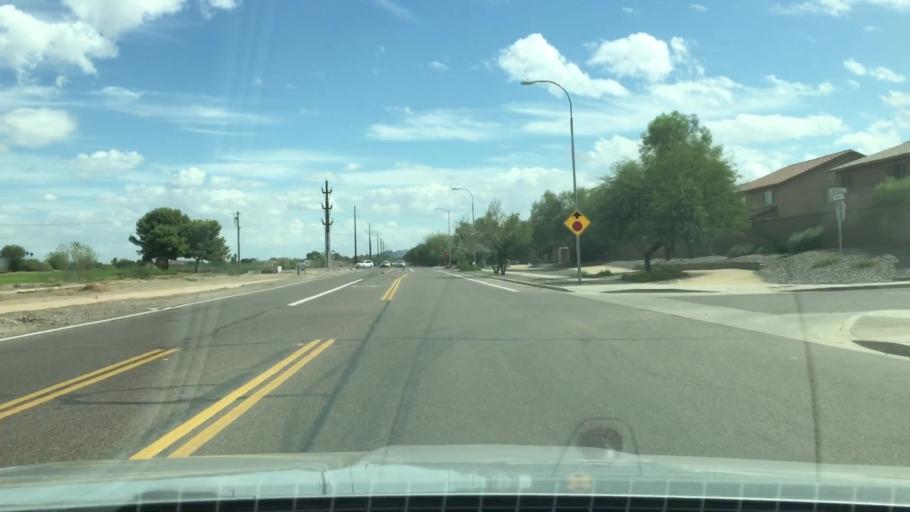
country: US
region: Arizona
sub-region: Maricopa County
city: Laveen
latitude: 33.3630
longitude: -112.1368
